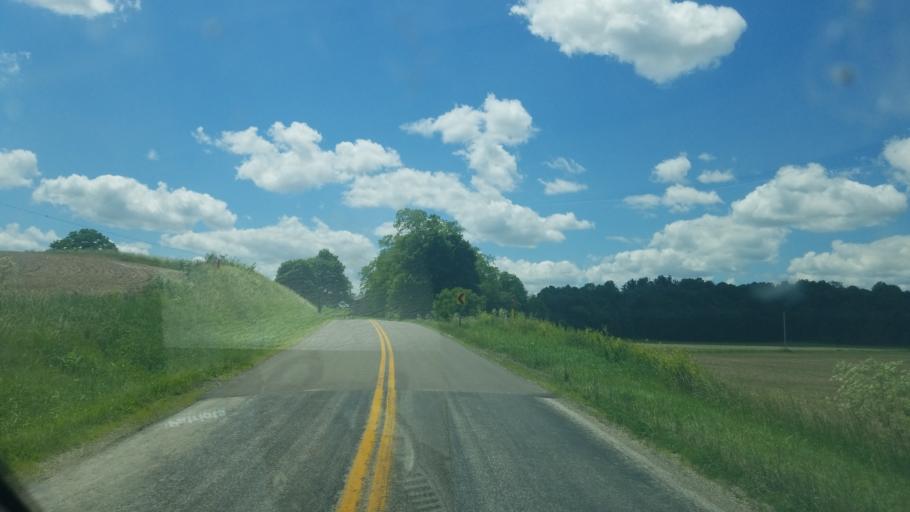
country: US
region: Ohio
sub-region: Ashland County
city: Ashland
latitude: 40.9674
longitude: -82.3806
